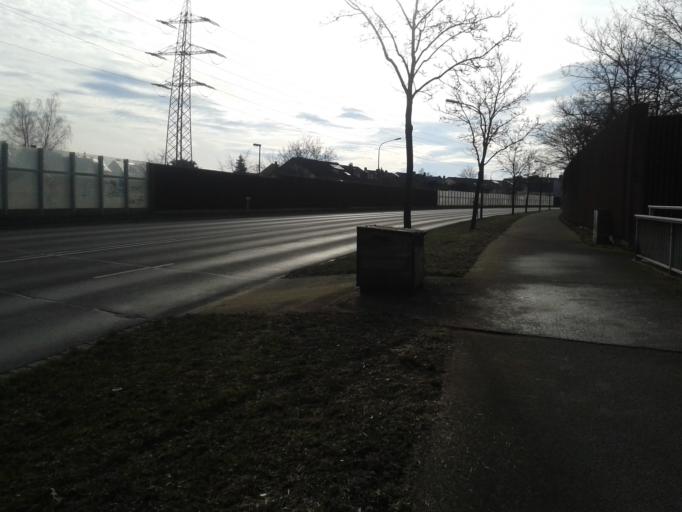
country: DE
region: Bavaria
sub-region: Upper Franconia
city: Bamberg
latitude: 49.9105
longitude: 10.9172
